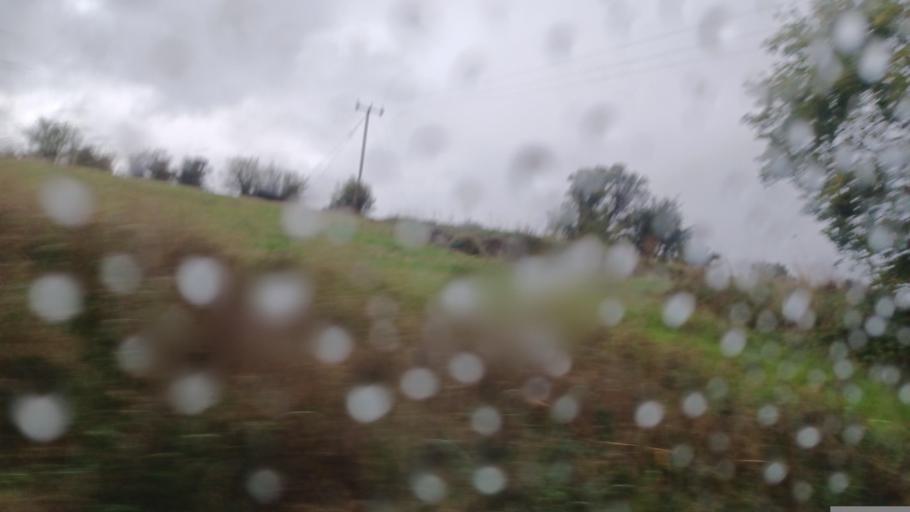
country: CY
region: Pafos
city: Mesogi
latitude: 34.8651
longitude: 32.5454
